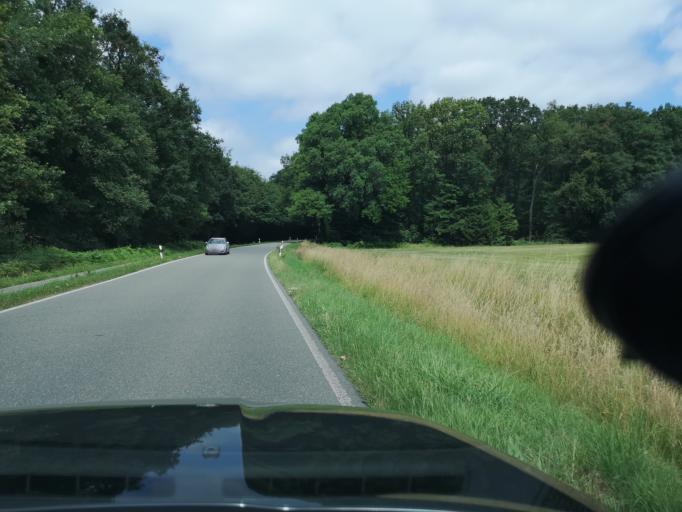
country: DE
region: North Rhine-Westphalia
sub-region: Regierungsbezirk Munster
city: Rhede
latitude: 51.8612
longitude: 6.6926
